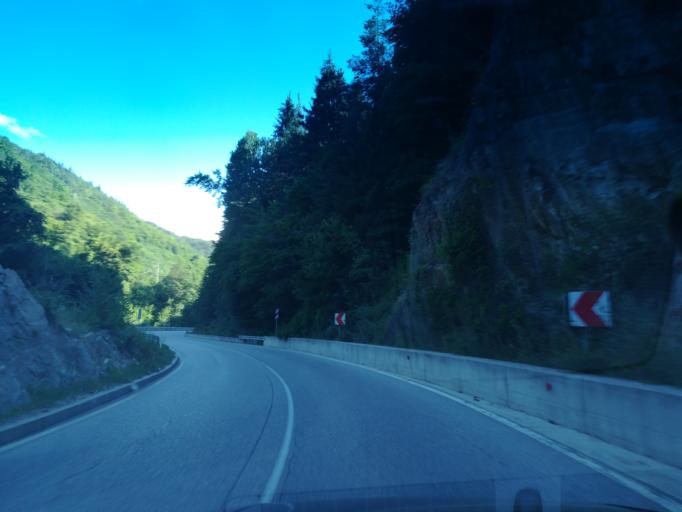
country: BG
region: Smolyan
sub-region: Obshtina Chepelare
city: Chepelare
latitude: 41.7818
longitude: 24.7071
